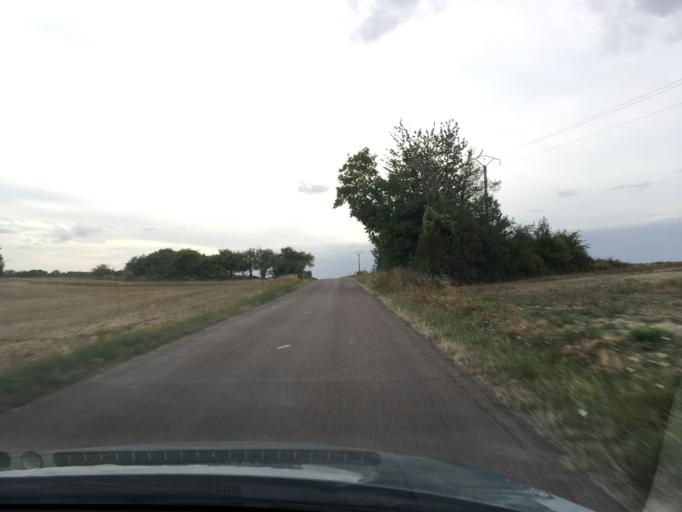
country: FR
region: Bourgogne
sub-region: Departement de l'Yonne
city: Fleury-la-Vallee
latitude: 47.8739
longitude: 3.4709
